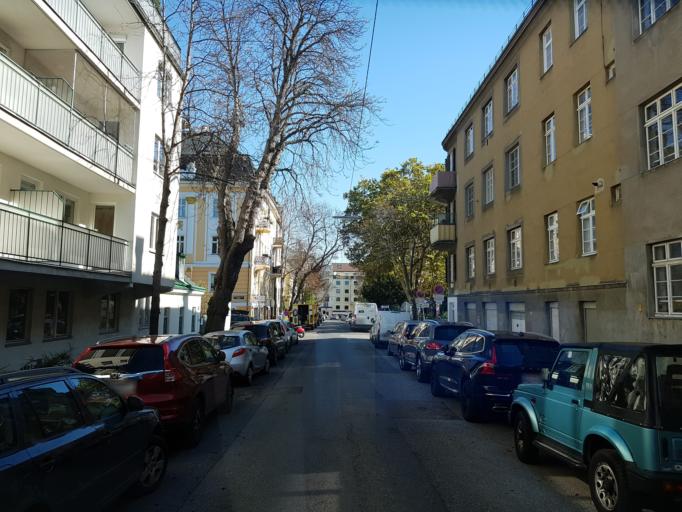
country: AT
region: Vienna
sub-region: Wien Stadt
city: Vienna
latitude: 48.2463
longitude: 16.3472
